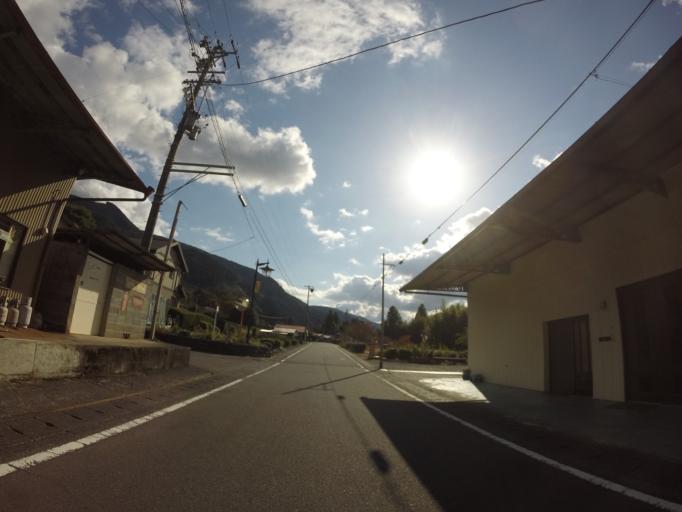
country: JP
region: Shizuoka
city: Kanaya
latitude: 35.0742
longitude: 138.1117
